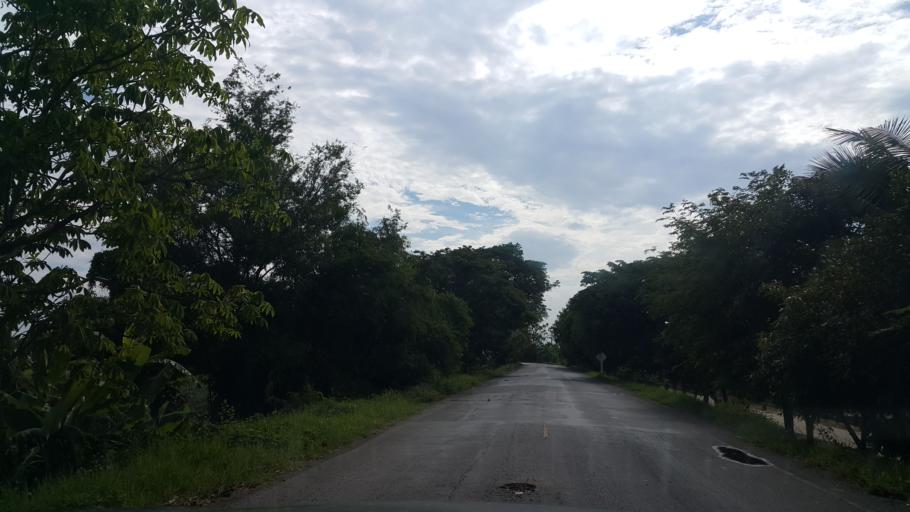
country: TH
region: Chiang Rai
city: Wiang Chai
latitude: 19.9599
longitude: 99.9415
